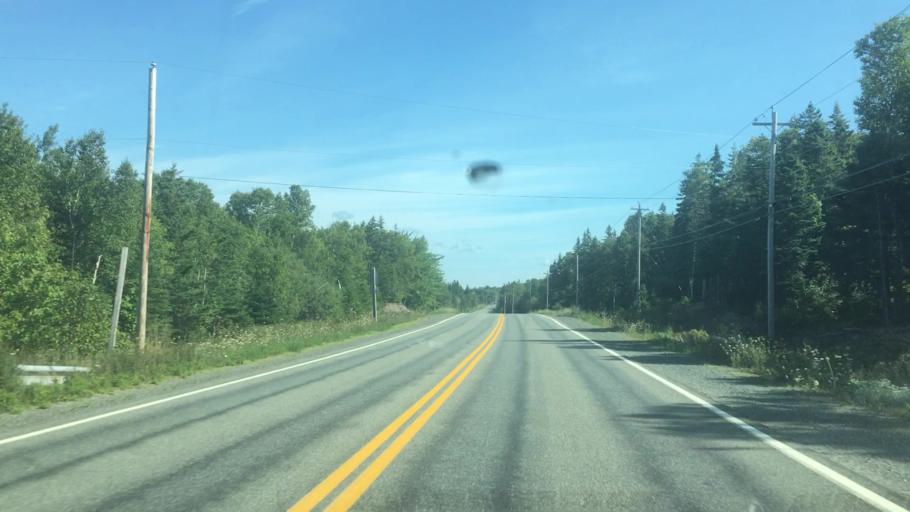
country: CA
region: Nova Scotia
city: Sydney
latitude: 45.9897
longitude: -60.4137
